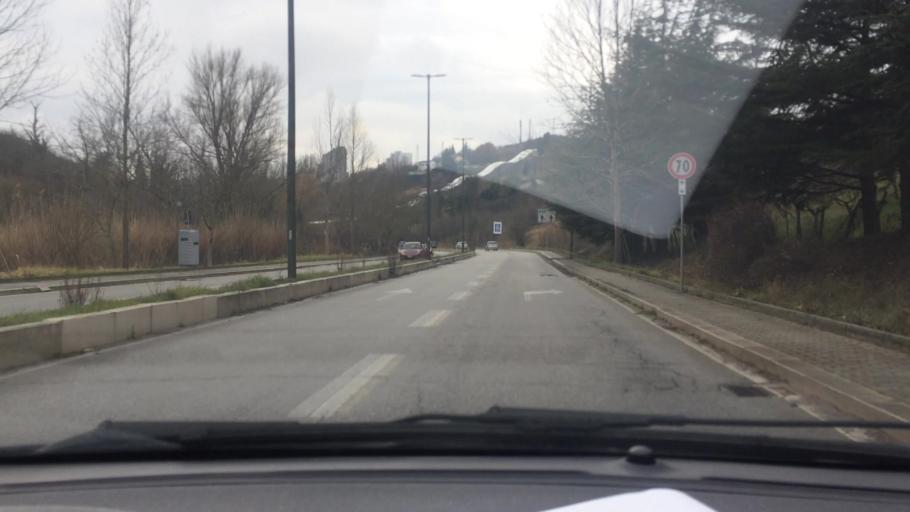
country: IT
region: Basilicate
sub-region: Provincia di Potenza
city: Potenza
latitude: 40.6406
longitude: 15.7982
